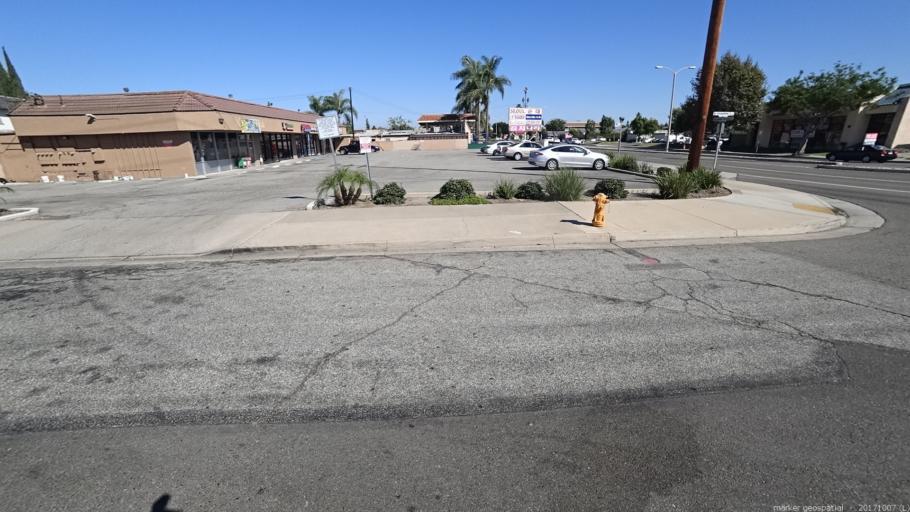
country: US
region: California
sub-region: Orange County
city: Midway City
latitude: 33.7742
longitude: -117.9796
